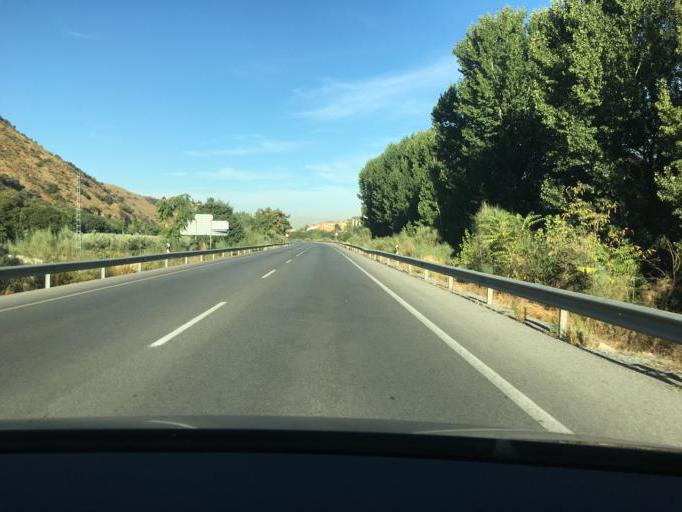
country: ES
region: Andalusia
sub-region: Provincia de Granada
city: Huetor Vega
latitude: 37.1602
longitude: -3.5590
